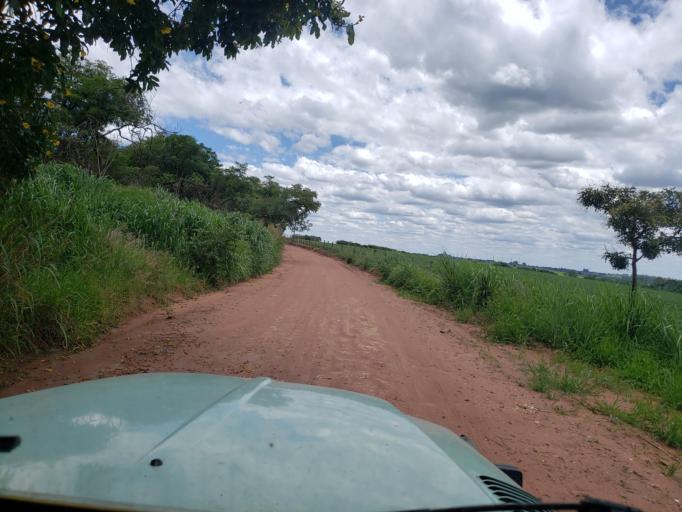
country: BR
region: Sao Paulo
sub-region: Aguai
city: Aguai
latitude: -22.1911
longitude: -46.9500
